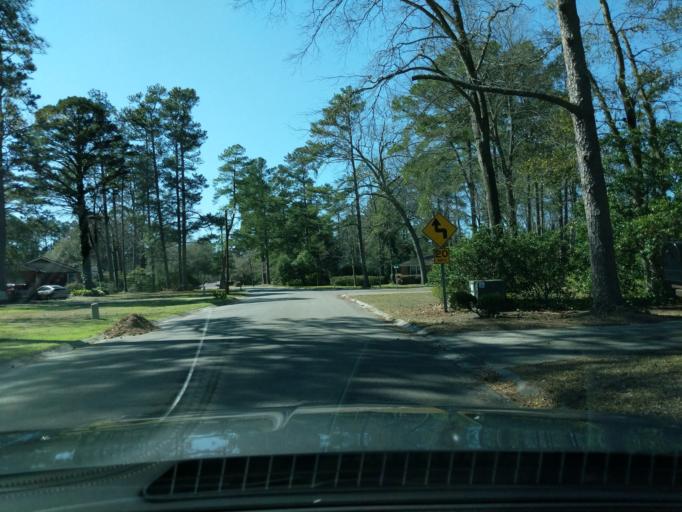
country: US
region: South Carolina
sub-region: Aiken County
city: Aiken
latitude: 33.5279
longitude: -81.7283
